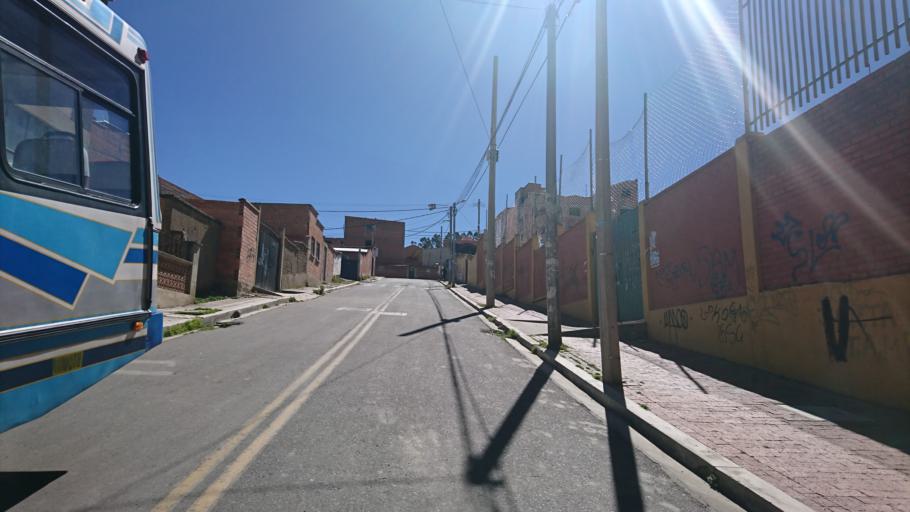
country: BO
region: La Paz
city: La Paz
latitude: -16.4916
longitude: -68.1042
